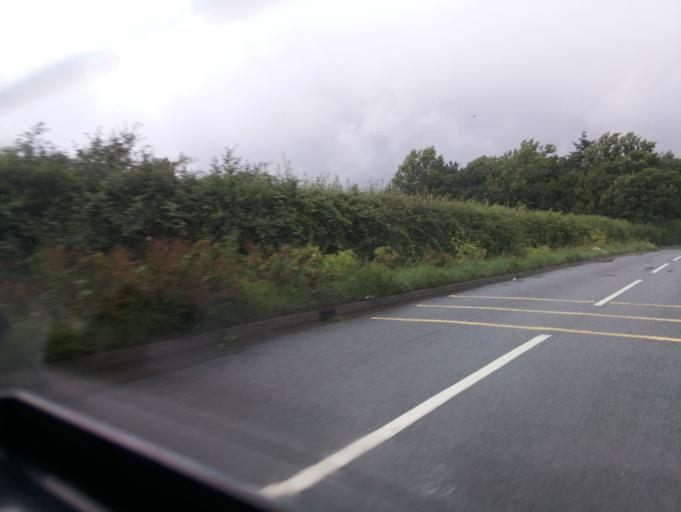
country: GB
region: England
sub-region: Gloucestershire
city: Uckington
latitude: 51.9598
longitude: -2.1348
